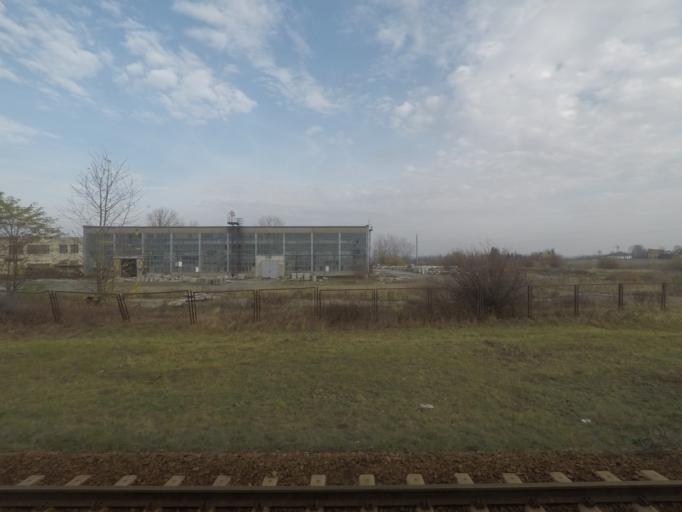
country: PL
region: Subcarpathian Voivodeship
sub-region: Powiat jaroslawski
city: Radymno
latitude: 49.9323
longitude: 22.8377
